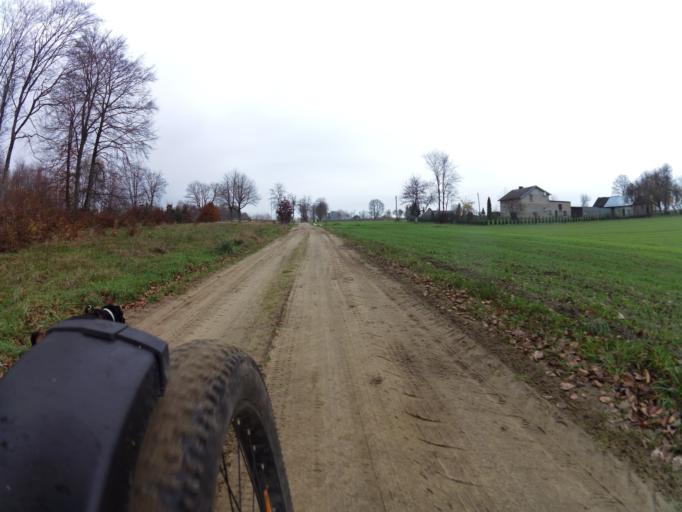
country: PL
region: Pomeranian Voivodeship
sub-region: Powiat pucki
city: Krokowa
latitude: 54.7166
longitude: 18.1387
